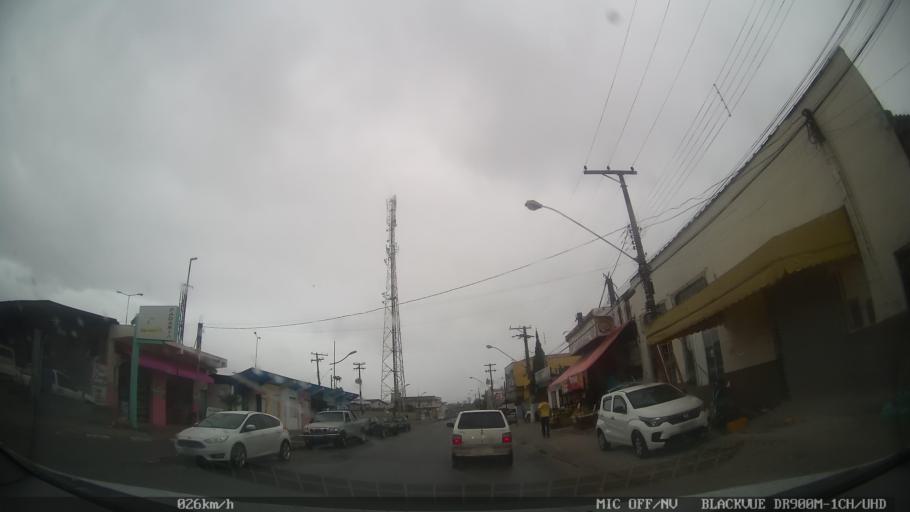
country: BR
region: Sao Paulo
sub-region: Juquia
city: Juquia
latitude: -24.3185
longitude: -47.6351
